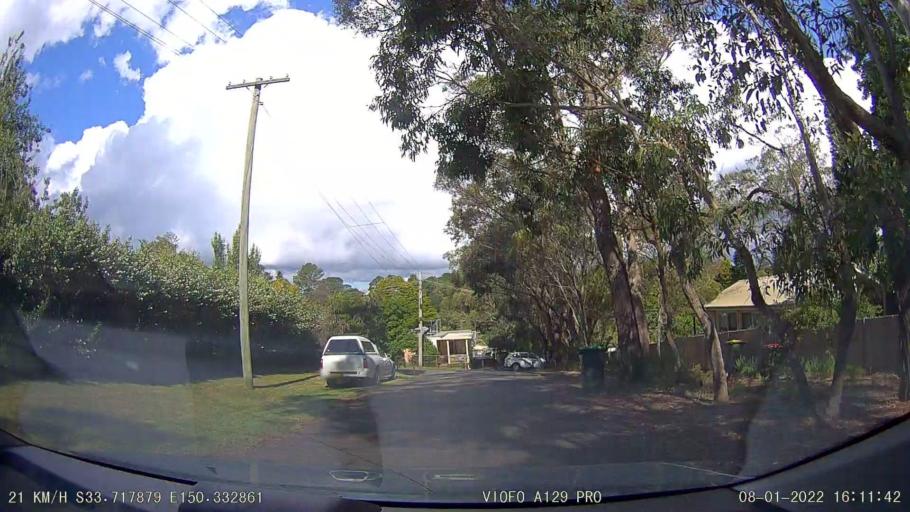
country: AU
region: New South Wales
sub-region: Blue Mountains Municipality
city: Leura
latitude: -33.7179
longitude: 150.3328
